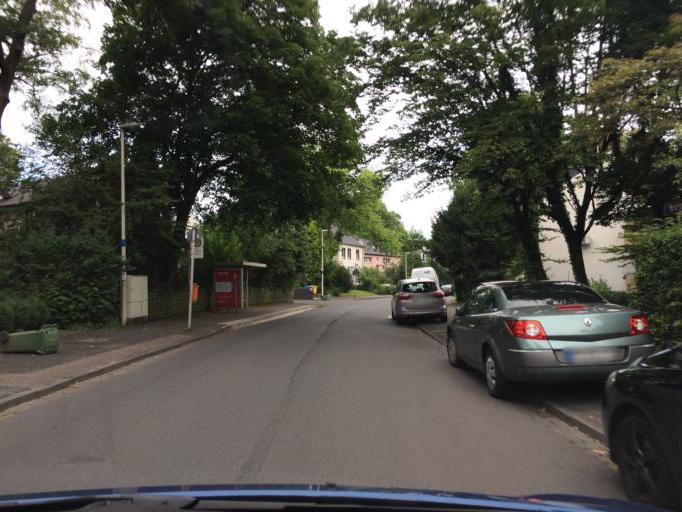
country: DE
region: North Rhine-Westphalia
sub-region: Regierungsbezirk Koln
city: Konigswinter
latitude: 50.6684
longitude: 7.1868
